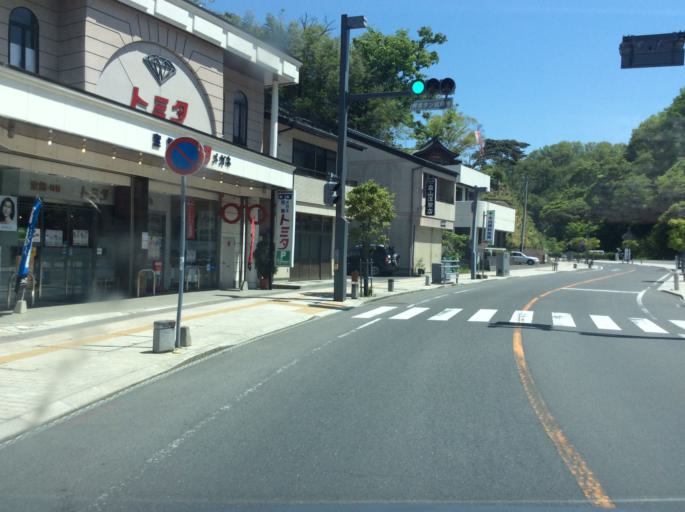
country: JP
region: Fukushima
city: Miharu
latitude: 37.4416
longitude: 140.4925
